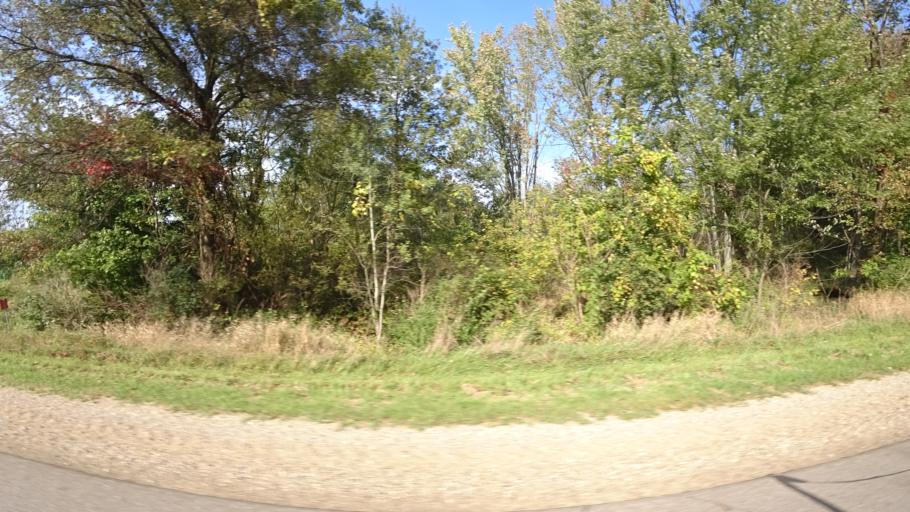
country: US
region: Michigan
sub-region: Saint Joseph County
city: Centreville
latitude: 42.0060
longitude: -85.5389
